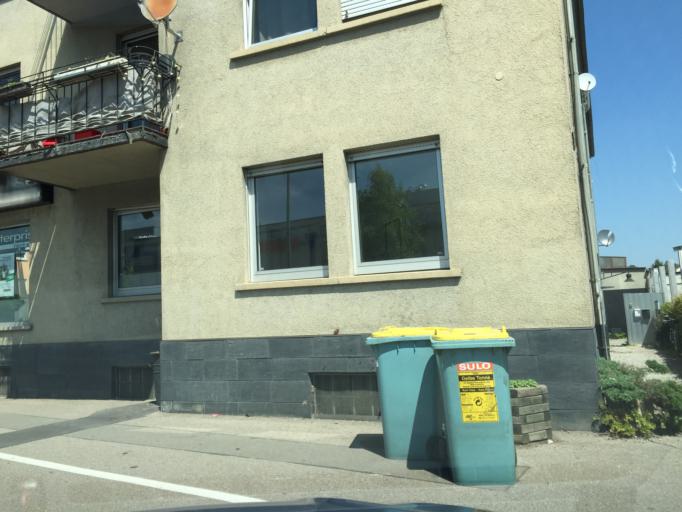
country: DE
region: Baden-Wuerttemberg
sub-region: Tuebingen Region
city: Ulm
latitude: 48.4004
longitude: 9.9631
